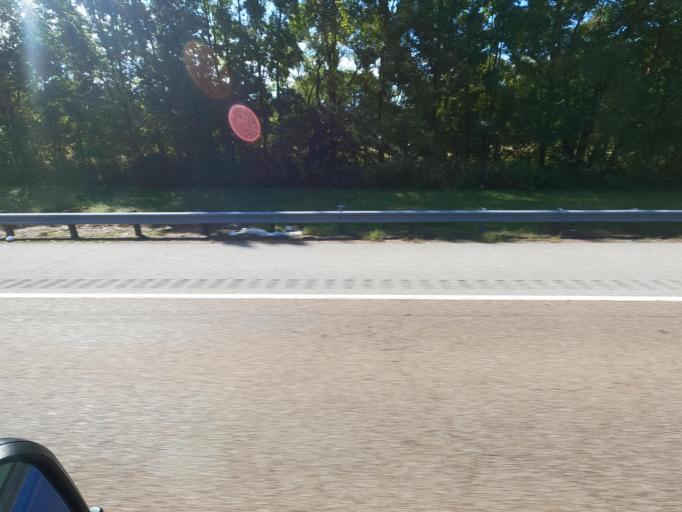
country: US
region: Tennessee
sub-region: Shelby County
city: Millington
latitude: 35.3096
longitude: -89.8477
